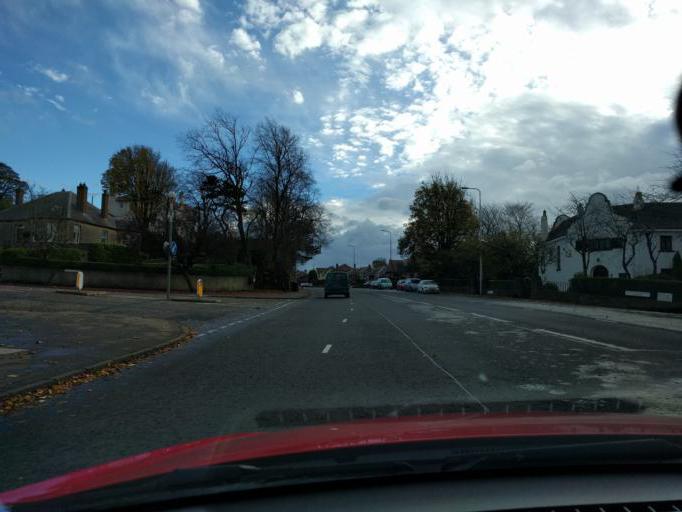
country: GB
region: Scotland
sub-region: Edinburgh
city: Edinburgh
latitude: 55.9127
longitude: -3.2134
